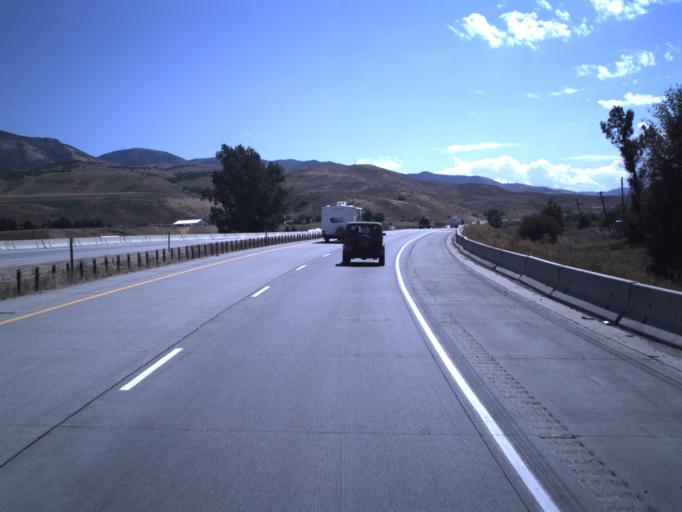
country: US
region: Utah
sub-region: Morgan County
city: Mountain Green
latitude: 41.1362
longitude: -111.7871
